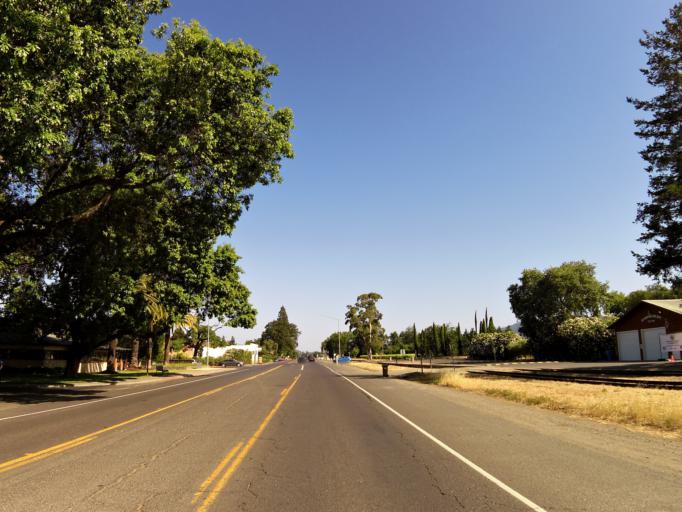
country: US
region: California
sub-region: Napa County
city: Saint Helena
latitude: 38.4595
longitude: -122.4235
